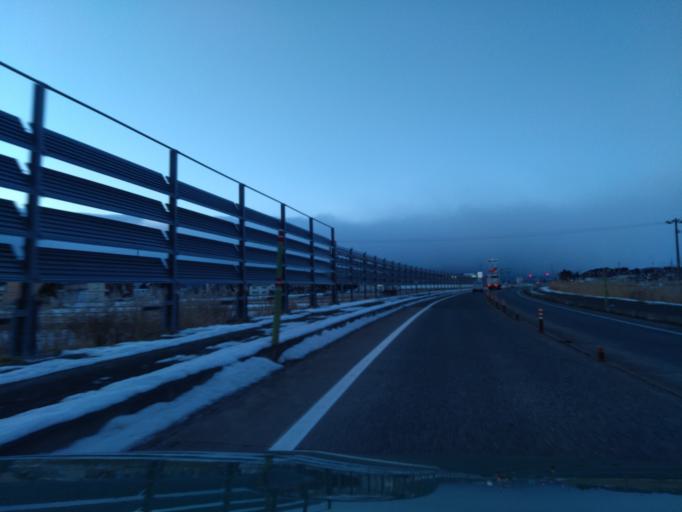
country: JP
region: Iwate
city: Shizukuishi
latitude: 39.6935
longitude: 140.9810
